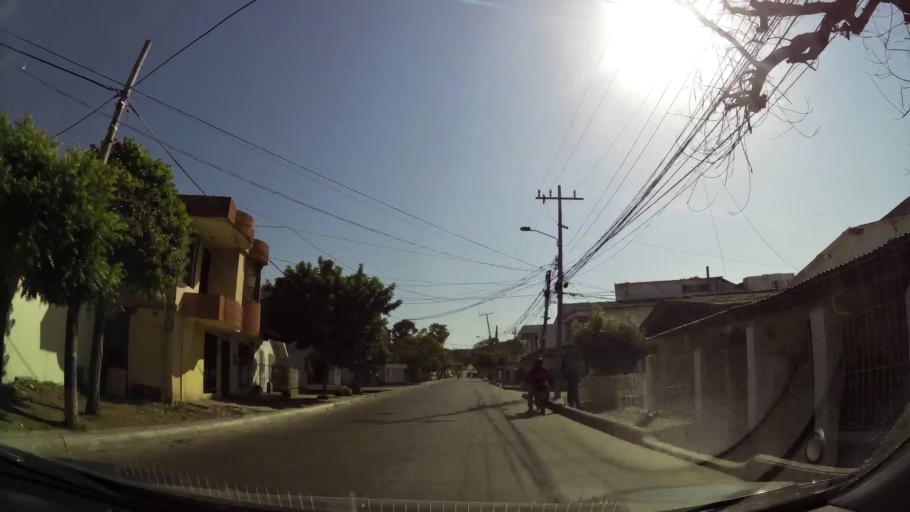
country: CO
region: Bolivar
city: Cartagena
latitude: 10.3998
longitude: -75.5174
